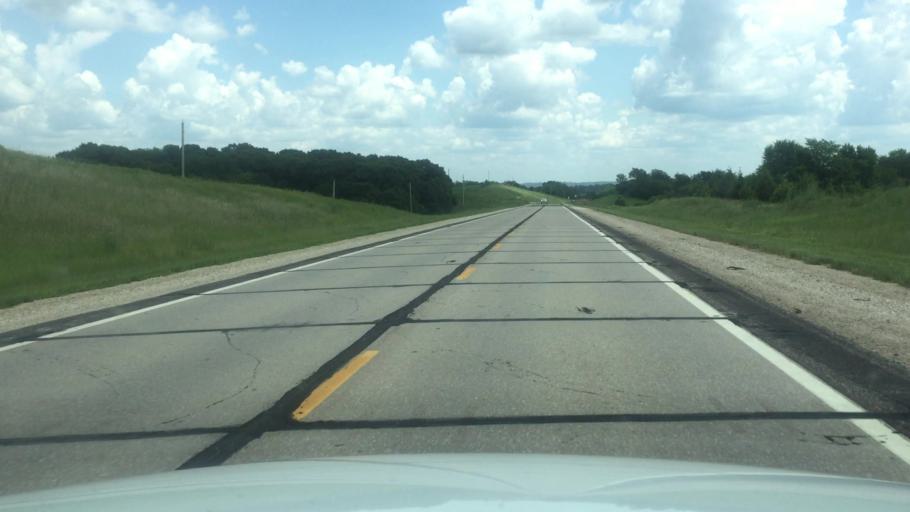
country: US
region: Kansas
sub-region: Atchison County
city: Atchison
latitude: 39.5572
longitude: -95.1682
